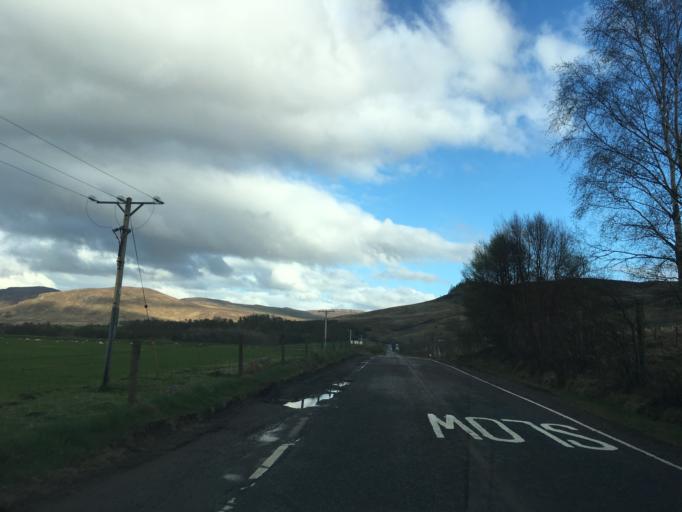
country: GB
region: Scotland
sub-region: Highland
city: Kingussie
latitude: 57.0125
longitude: -4.2718
